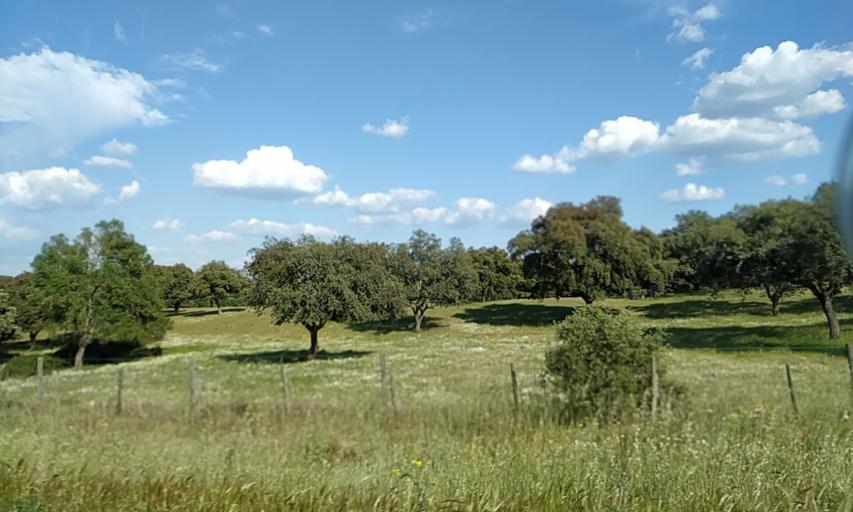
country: PT
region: Portalegre
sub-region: Fronteira
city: Fronteira
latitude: 38.9936
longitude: -7.4736
